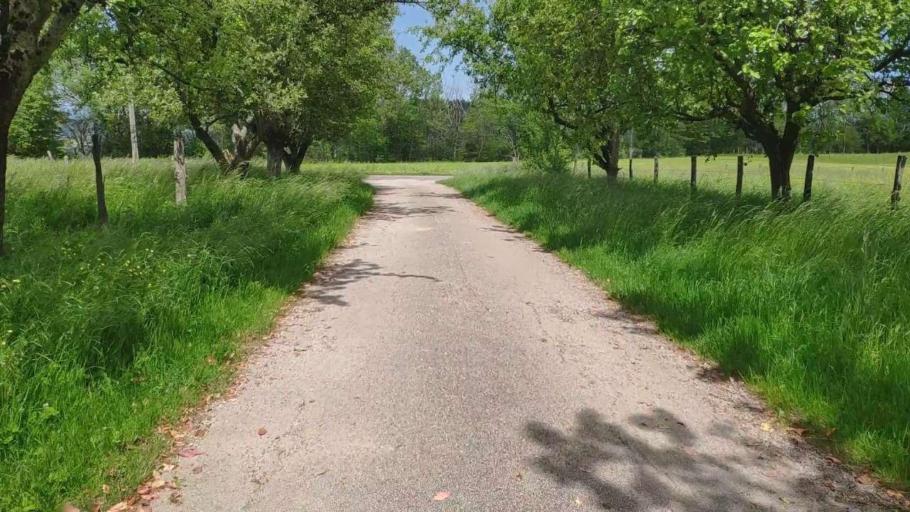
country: FR
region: Franche-Comte
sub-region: Departement du Jura
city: Poligny
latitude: 46.7586
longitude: 5.6362
